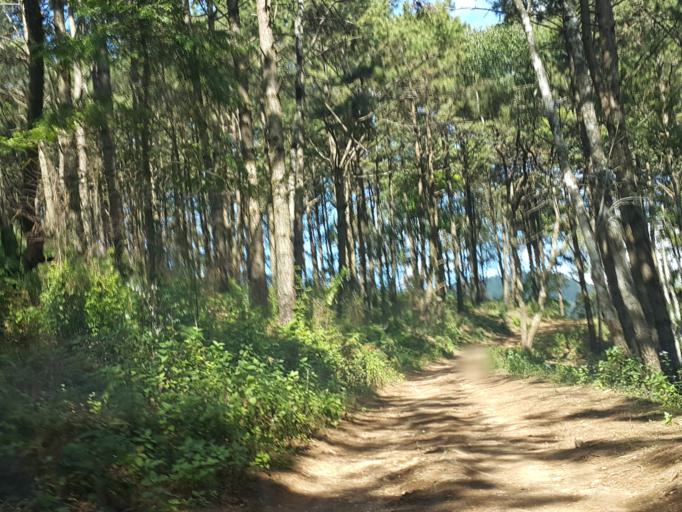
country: TH
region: Chiang Mai
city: Wiang Haeng
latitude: 19.5393
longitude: 98.8145
